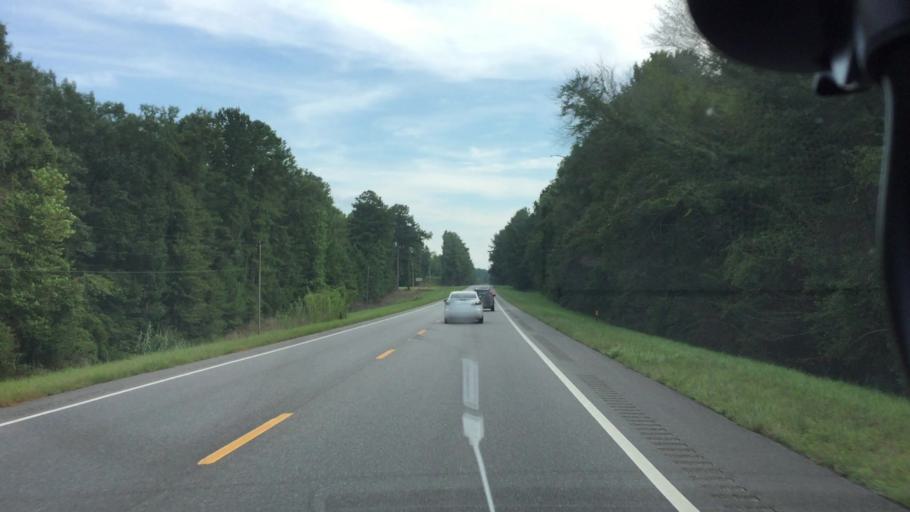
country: US
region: Alabama
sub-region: Coffee County
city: New Brockton
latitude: 31.5639
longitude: -85.9251
